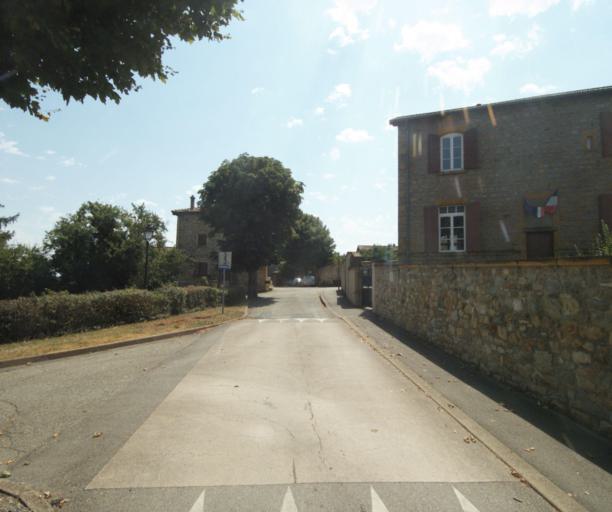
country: FR
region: Rhone-Alpes
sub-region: Departement du Rhone
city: Saint-Germain-Nuelles
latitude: 45.8486
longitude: 4.6242
